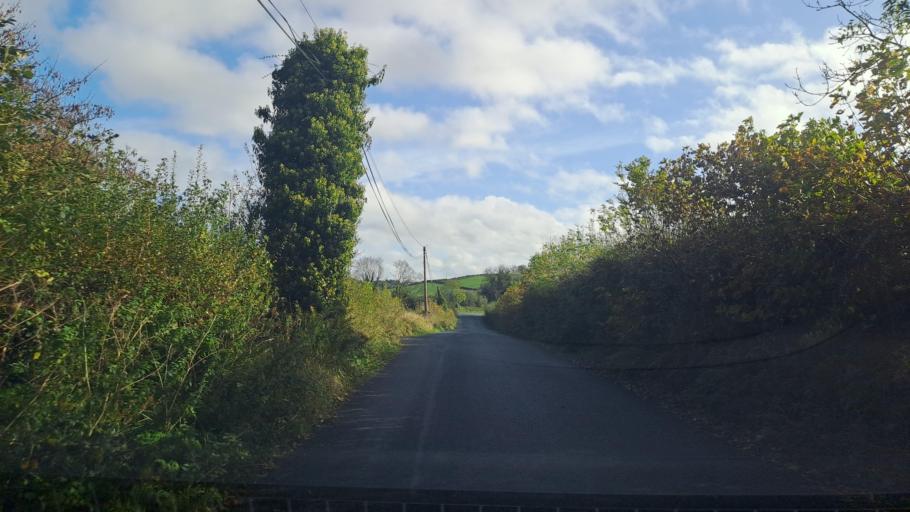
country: IE
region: Ulster
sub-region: An Cabhan
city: Bailieborough
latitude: 53.9917
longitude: -7.0198
